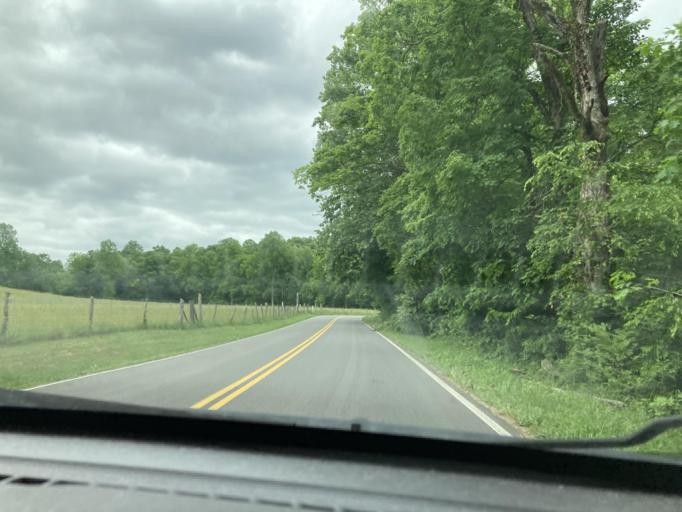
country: US
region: Tennessee
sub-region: Dickson County
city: Dickson
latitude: 36.0411
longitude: -87.3679
